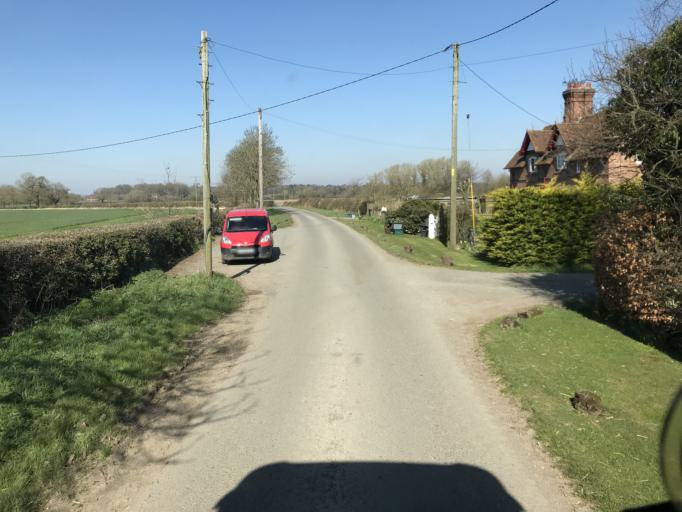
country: GB
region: England
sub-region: Cheshire West and Chester
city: Aldford
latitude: 53.1255
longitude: -2.8518
